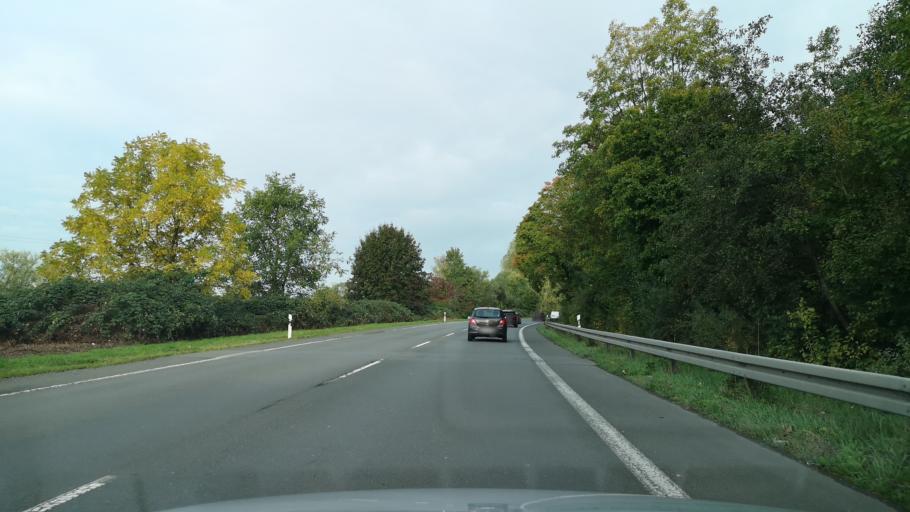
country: DE
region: North Rhine-Westphalia
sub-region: Regierungsbezirk Arnsberg
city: Hagen
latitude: 51.3939
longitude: 7.5130
